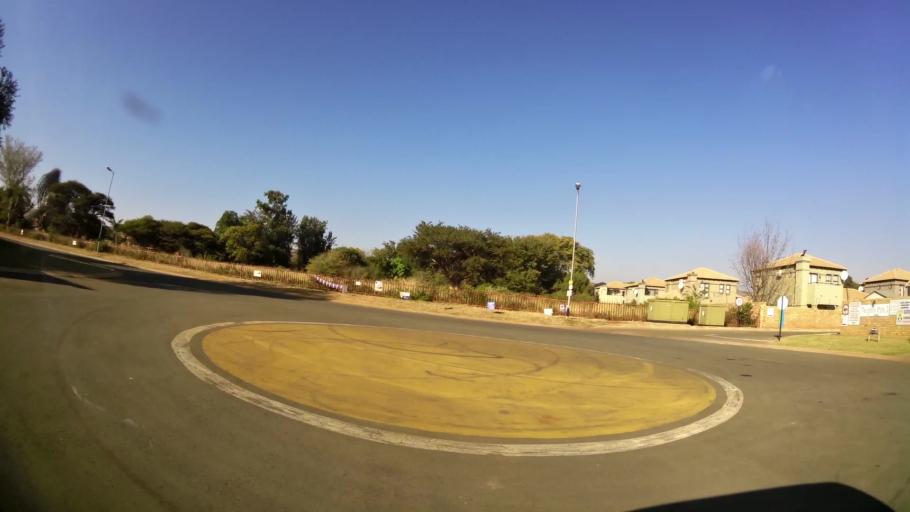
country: ZA
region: Gauteng
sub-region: City of Tshwane Metropolitan Municipality
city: Pretoria
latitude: -25.6694
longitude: 28.2020
